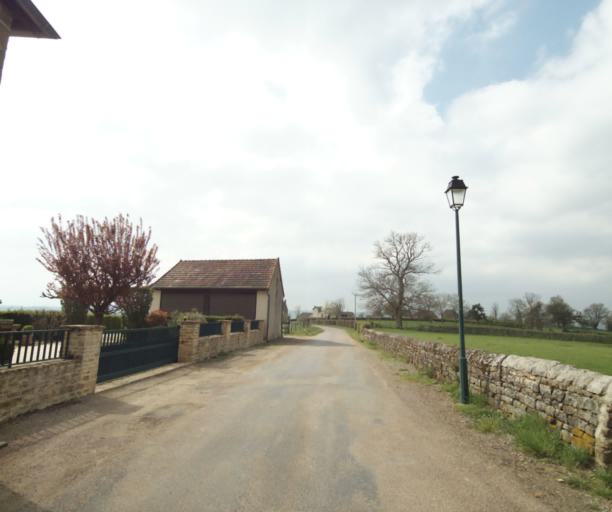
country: FR
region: Bourgogne
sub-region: Departement de Saone-et-Loire
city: Charolles
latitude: 46.3557
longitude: 4.2206
